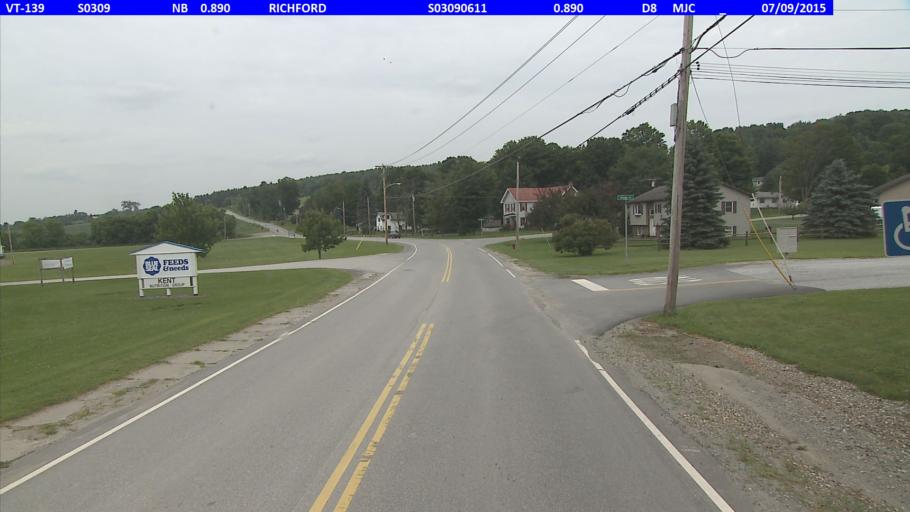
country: US
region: Vermont
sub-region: Franklin County
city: Richford
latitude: 45.0017
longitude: -72.6628
